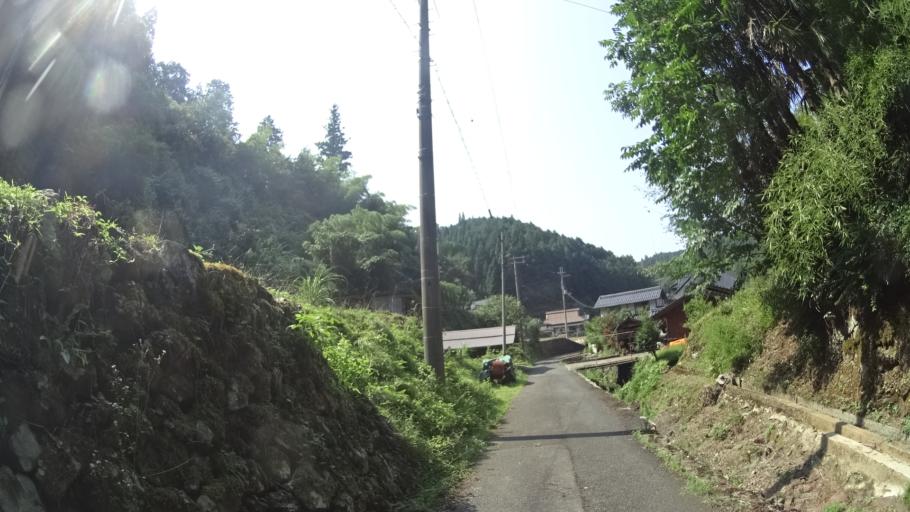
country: JP
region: Kyoto
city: Ayabe
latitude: 35.3997
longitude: 135.2150
